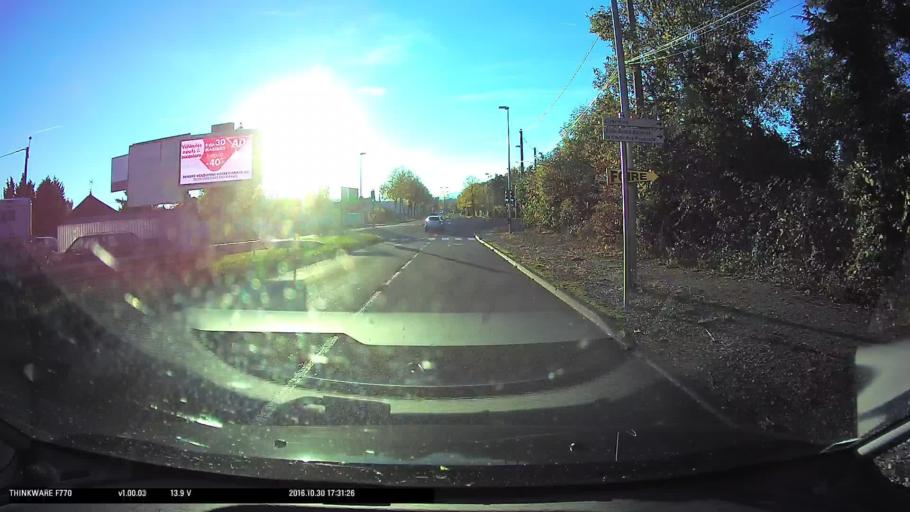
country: FR
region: Bourgogne
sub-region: Departement de la Cote-d'Or
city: Longvic
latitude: 47.3023
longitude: 5.0683
